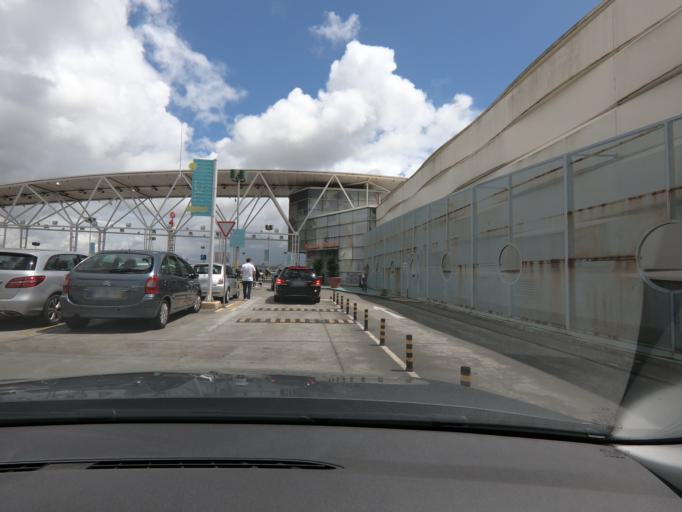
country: PT
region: Lisbon
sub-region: Cascais
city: Alcabideche
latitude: 38.7390
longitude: -9.3995
